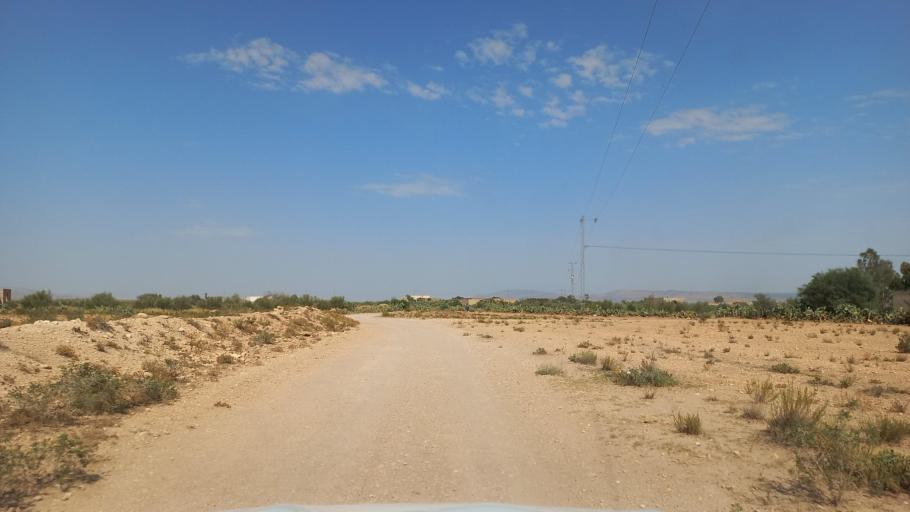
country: TN
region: Al Qasrayn
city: Kasserine
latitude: 35.2787
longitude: 8.9541
